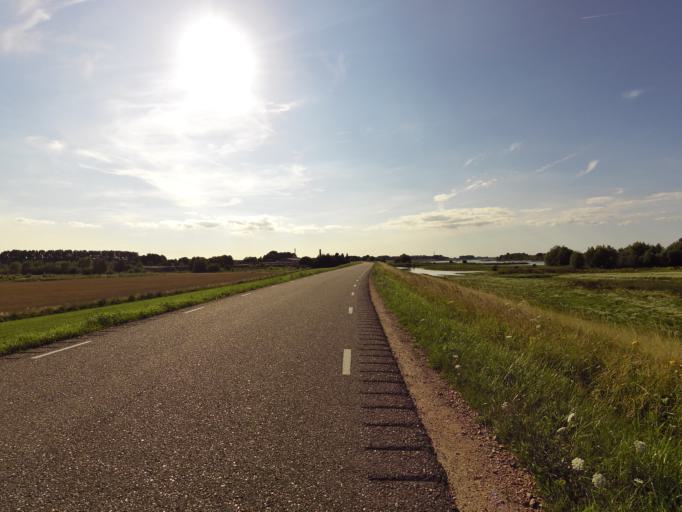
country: NL
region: Gelderland
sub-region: Gemeente Groesbeek
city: Berg en Dal
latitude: 51.8491
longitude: 5.9740
